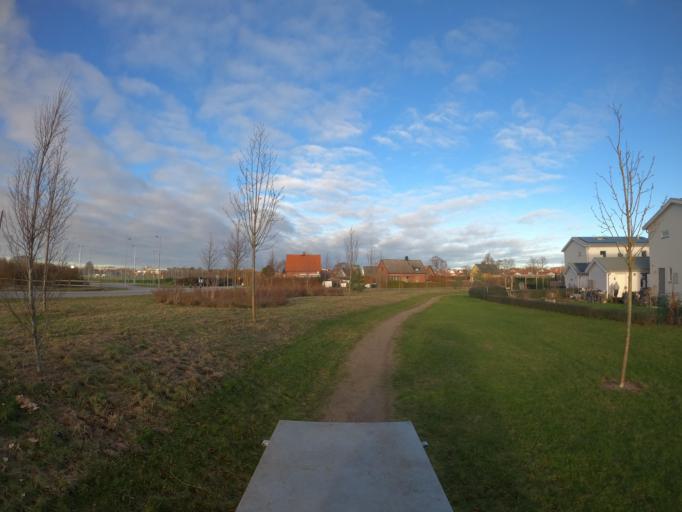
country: SE
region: Skane
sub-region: Svedala Kommun
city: Svedala
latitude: 55.5010
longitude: 13.2396
